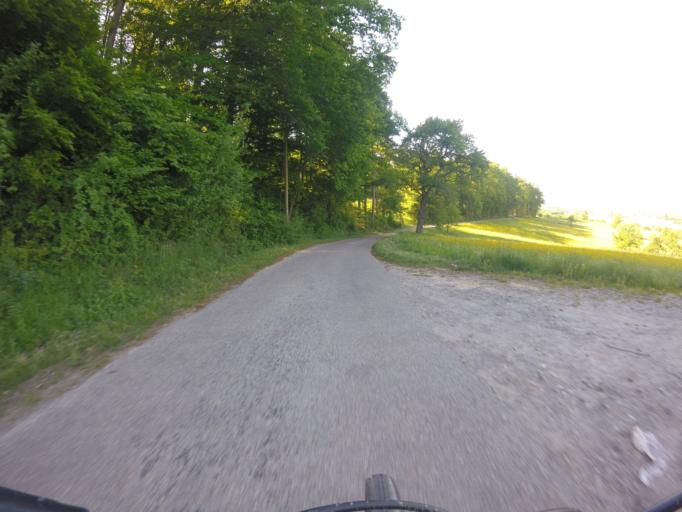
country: DE
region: Baden-Wuerttemberg
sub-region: Regierungsbezirk Stuttgart
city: Aspach
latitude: 48.9860
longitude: 9.4158
